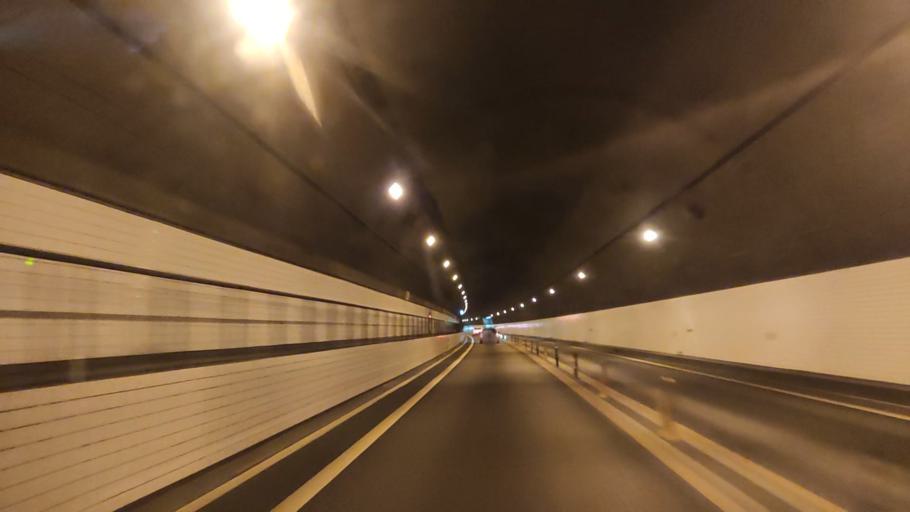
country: JP
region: Tokushima
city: Ikedacho
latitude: 34.0227
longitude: 133.7705
